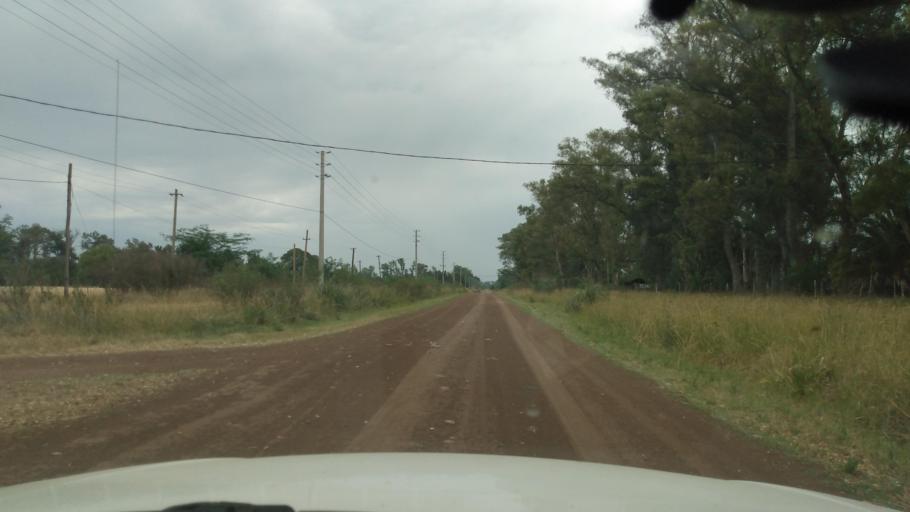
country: AR
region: Buenos Aires
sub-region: Partido de Lujan
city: Lujan
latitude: -34.5528
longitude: -59.1729
